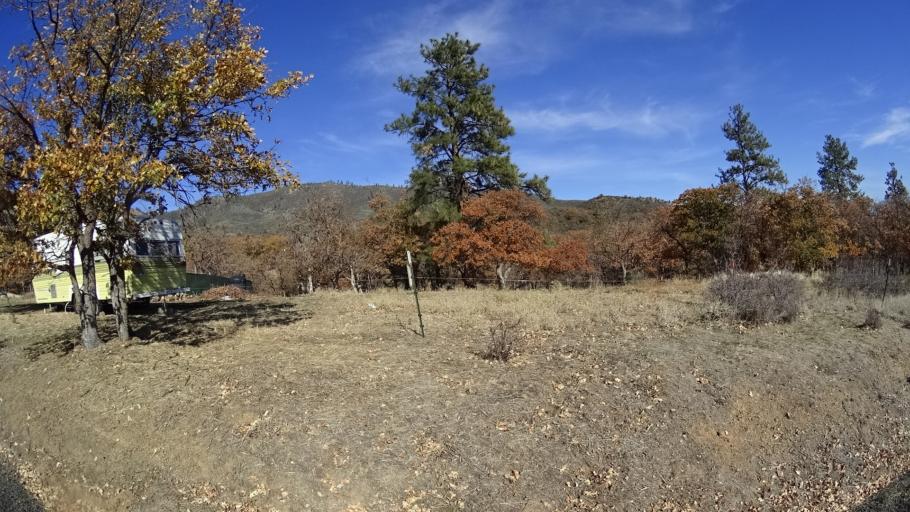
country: US
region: California
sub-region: Siskiyou County
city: Yreka
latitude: 41.7752
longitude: -122.6510
